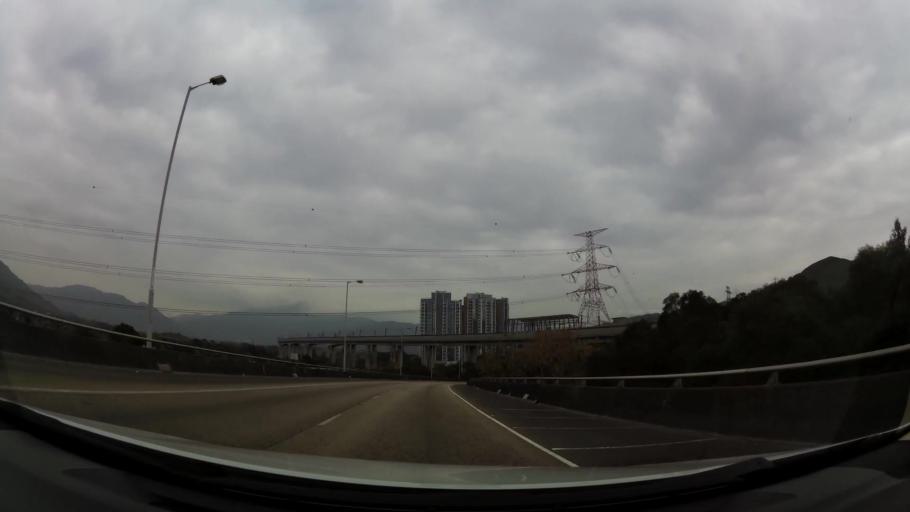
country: HK
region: Yuen Long
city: Yuen Long Kau Hui
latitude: 22.4478
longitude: 114.0492
